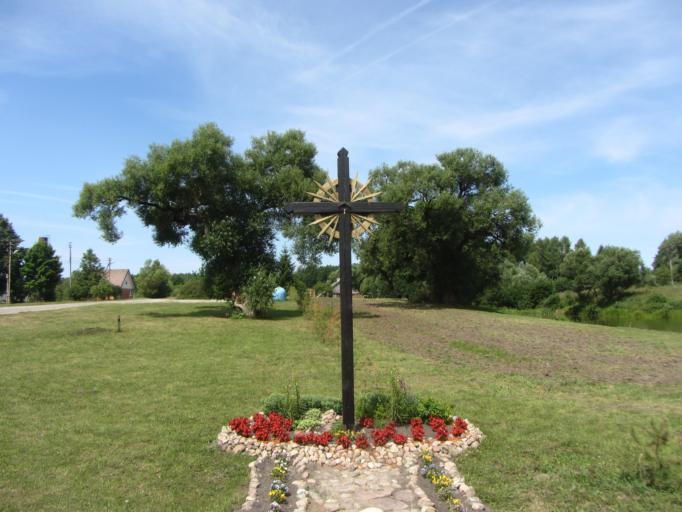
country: LT
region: Alytaus apskritis
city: Druskininkai
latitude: 54.1048
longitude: 24.1109
